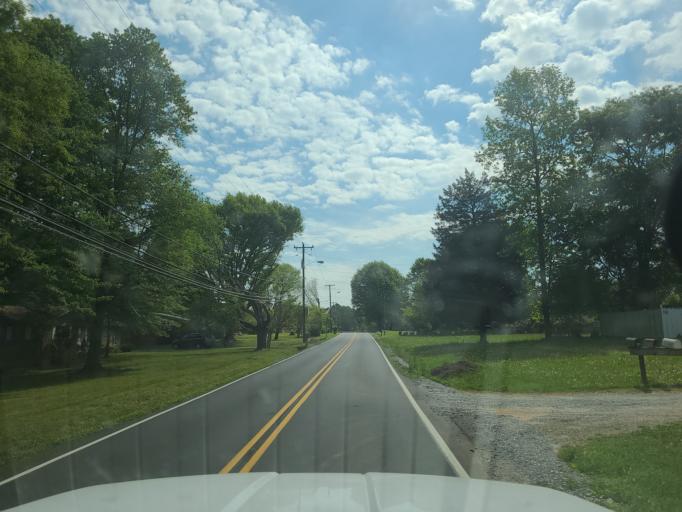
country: US
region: North Carolina
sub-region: Cleveland County
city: Shelby
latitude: 35.2919
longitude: -81.4935
